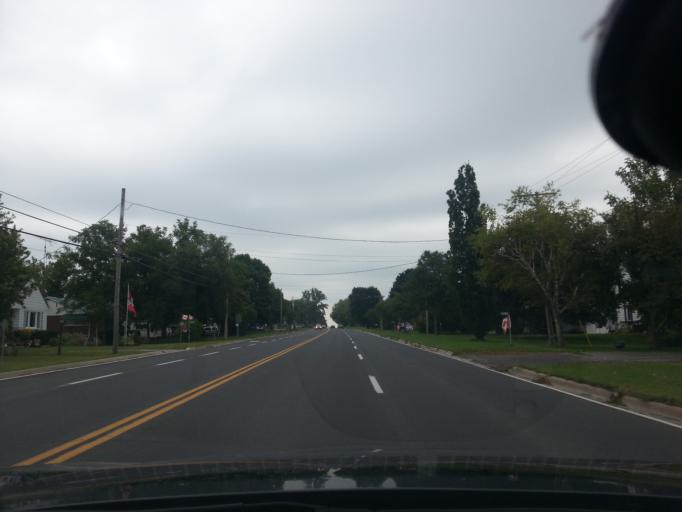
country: CA
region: Ontario
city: Picton
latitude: 43.9959
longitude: -77.1737
